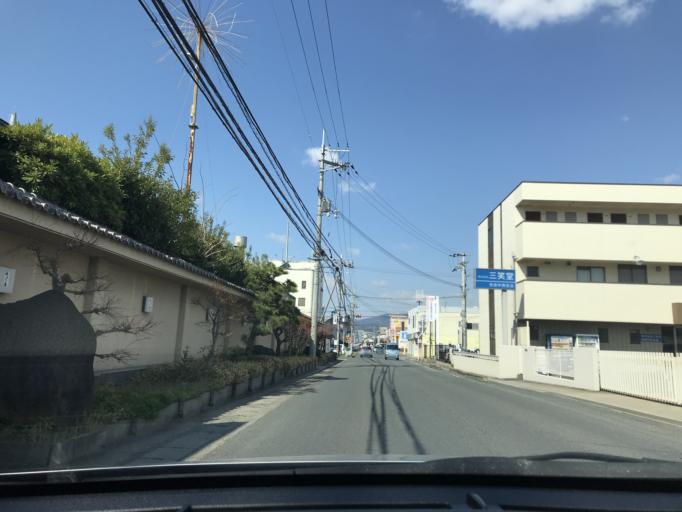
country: JP
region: Nara
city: Nara-shi
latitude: 34.6699
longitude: 135.8026
